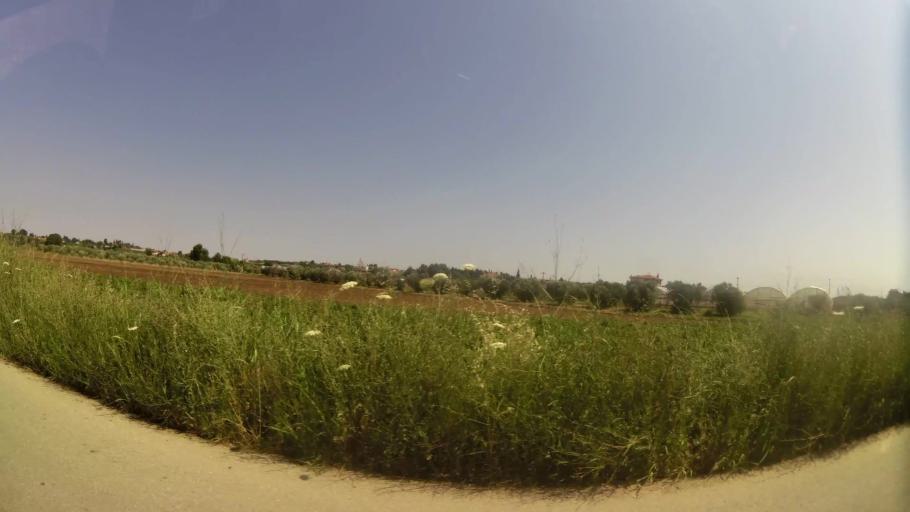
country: GR
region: Central Macedonia
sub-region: Nomos Thessalonikis
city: Nea Michaniona
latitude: 40.4916
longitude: 22.8289
